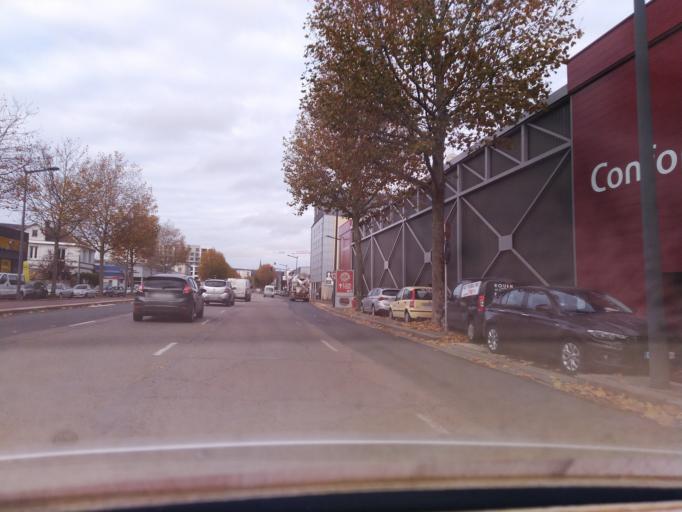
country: FR
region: Haute-Normandie
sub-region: Departement de la Seine-Maritime
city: Rouen
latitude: 49.4457
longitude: 1.0723
